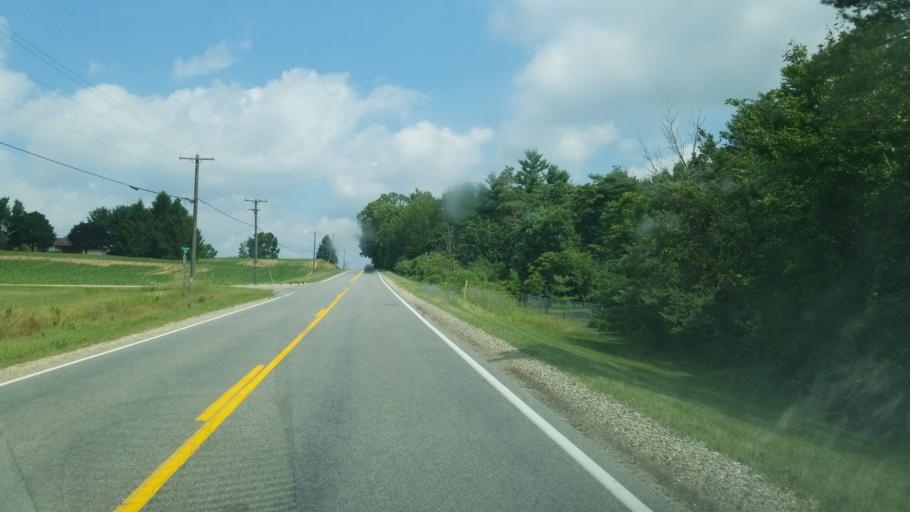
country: US
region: Michigan
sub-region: Kent County
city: Kent City
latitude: 43.2118
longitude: -85.7114
